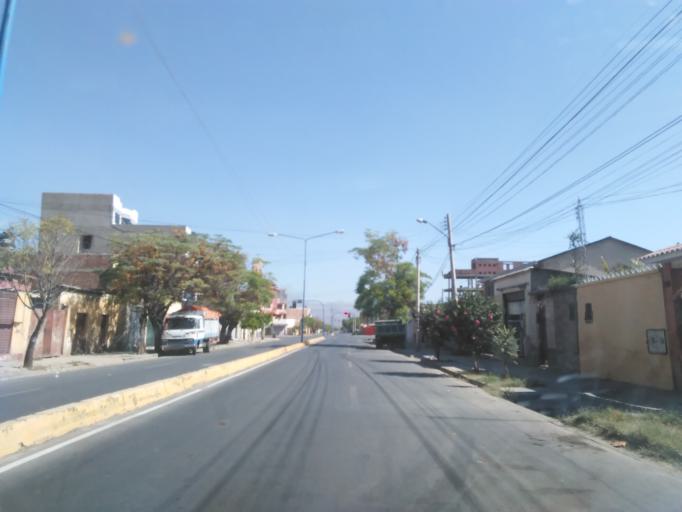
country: BO
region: Cochabamba
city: Cochabamba
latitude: -17.4161
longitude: -66.1639
